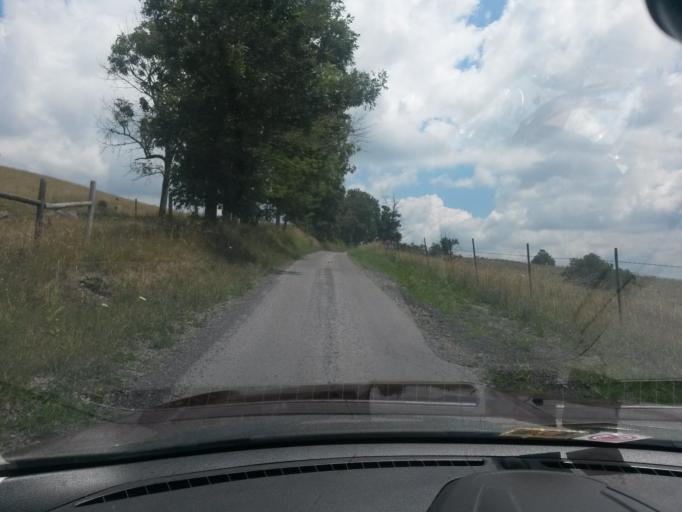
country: US
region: West Virginia
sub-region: Monroe County
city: Union
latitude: 37.5570
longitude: -80.5150
